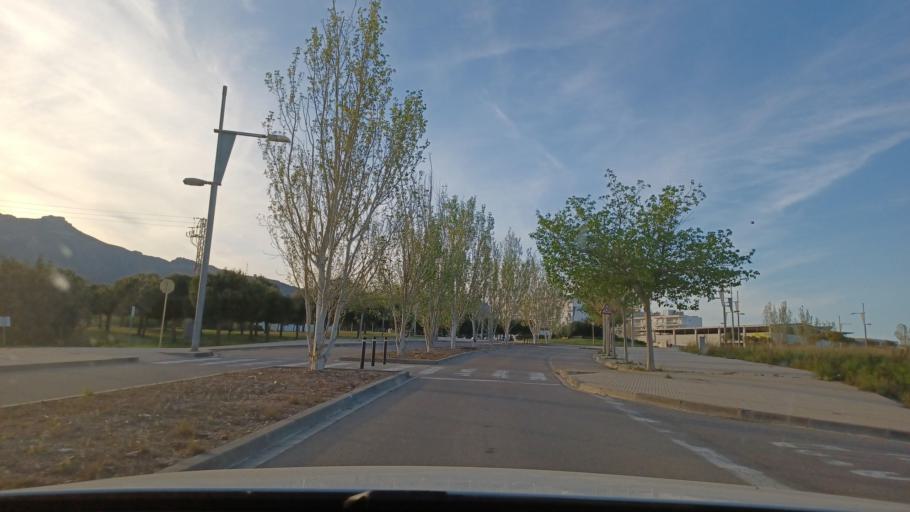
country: ES
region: Catalonia
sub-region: Provincia de Tarragona
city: Sant Carles de la Rapita
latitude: 40.6160
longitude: 0.5805
